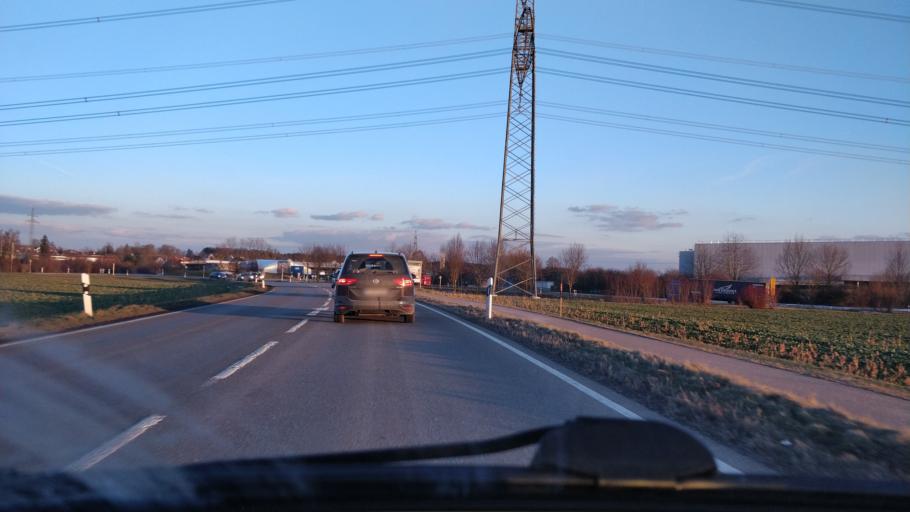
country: DE
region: Bavaria
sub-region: Swabia
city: Pfaffenhofen an der Roth
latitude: 48.3606
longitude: 10.1505
